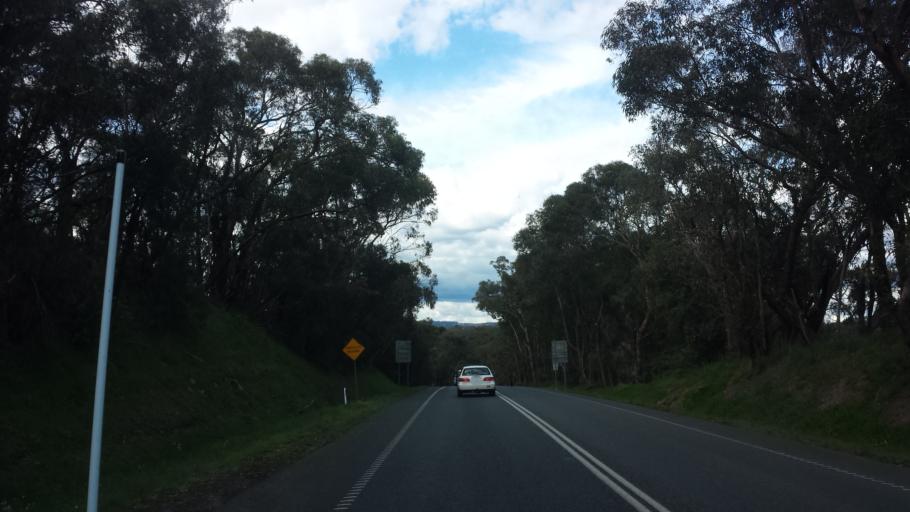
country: AU
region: Victoria
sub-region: Yarra Ranges
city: Belgrave South
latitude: -37.9610
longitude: 145.3630
